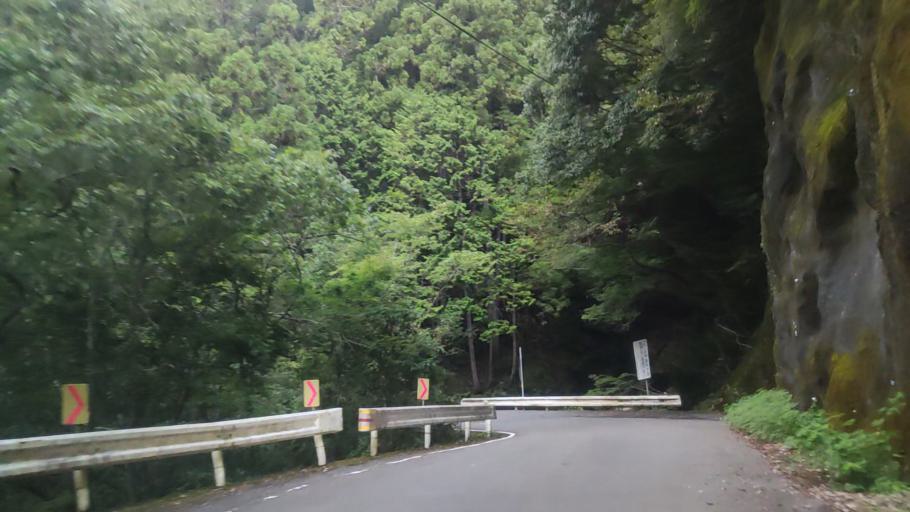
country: JP
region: Wakayama
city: Hashimoto
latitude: 34.2709
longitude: 135.6387
